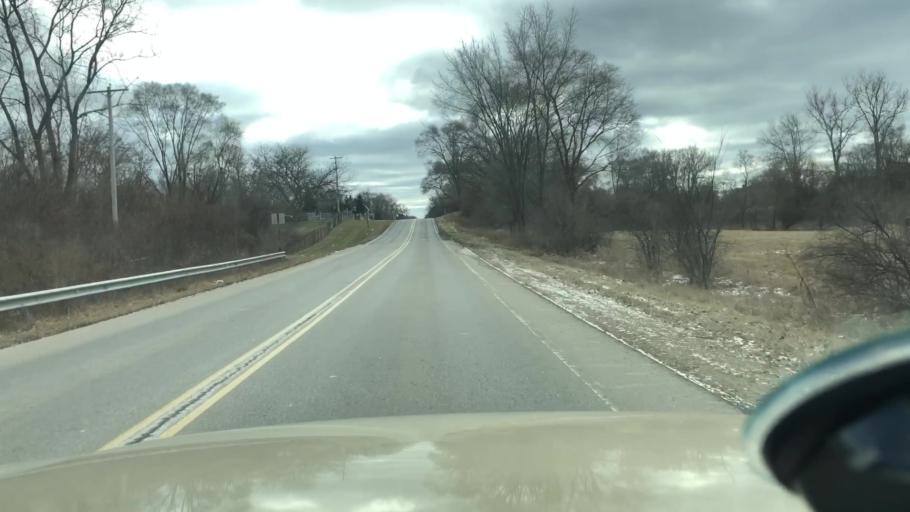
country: US
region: Michigan
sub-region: Jackson County
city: Jackson
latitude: 42.2751
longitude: -84.3649
